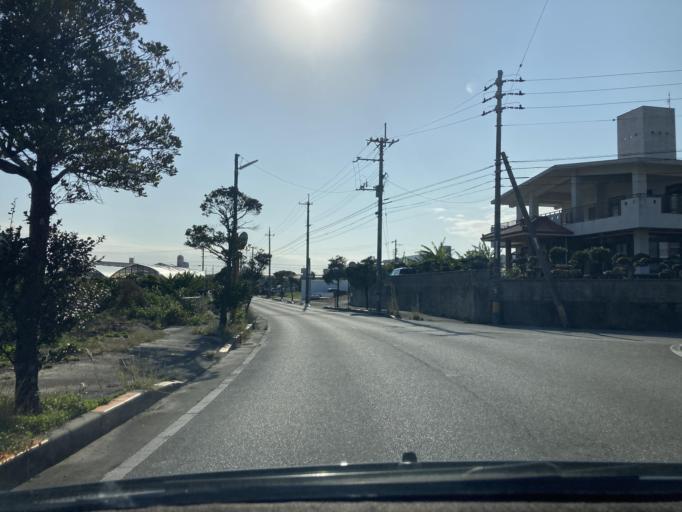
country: JP
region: Okinawa
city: Tomigusuku
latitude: 26.1690
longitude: 127.6571
